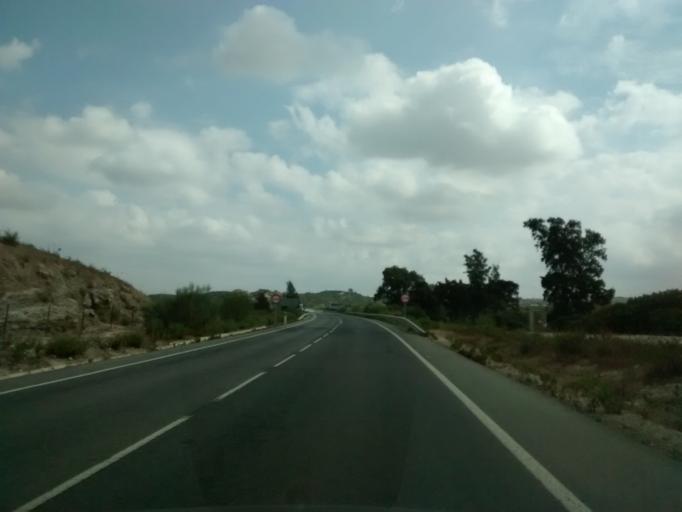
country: ES
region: Andalusia
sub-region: Provincia de Cadiz
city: Medina Sidonia
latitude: 36.4327
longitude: -6.0361
